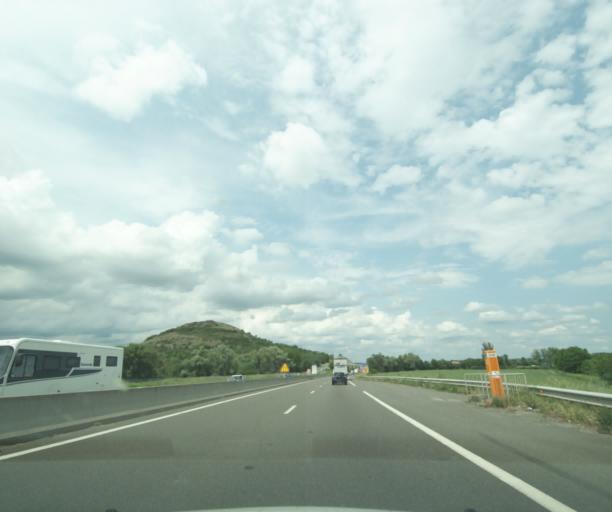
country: FR
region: Auvergne
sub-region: Departement du Puy-de-Dome
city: Aubiere
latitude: 45.7670
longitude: 3.1388
